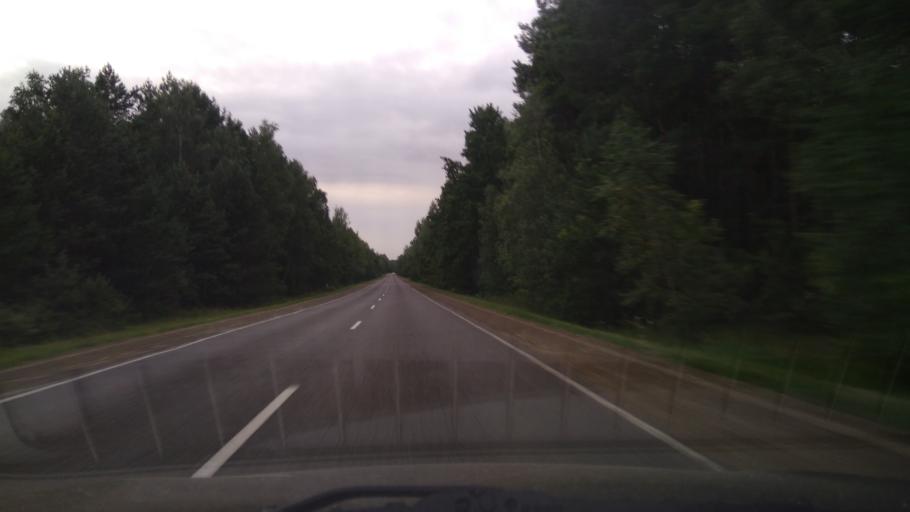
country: BY
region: Brest
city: Byaroza
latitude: 52.4064
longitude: 24.9986
